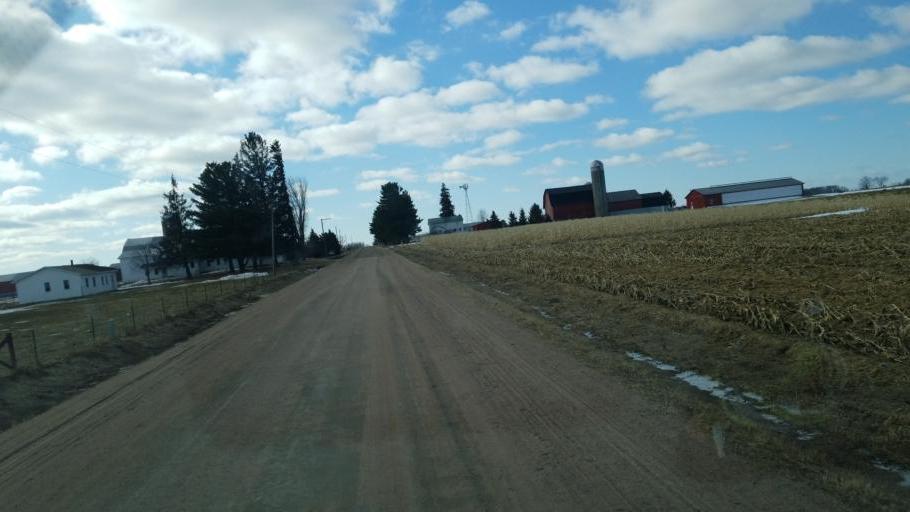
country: US
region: Wisconsin
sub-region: Clark County
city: Loyal
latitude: 44.6491
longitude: -90.3977
